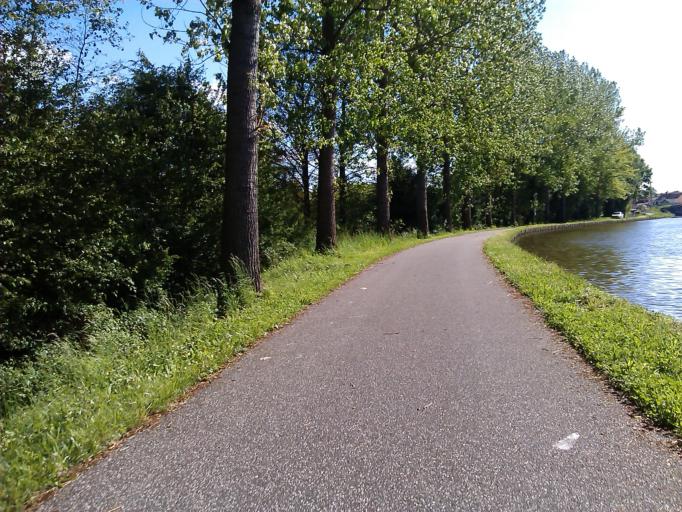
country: FR
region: Bourgogne
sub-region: Departement de Saone-et-Loire
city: Ecuisses
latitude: 46.7640
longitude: 4.5237
